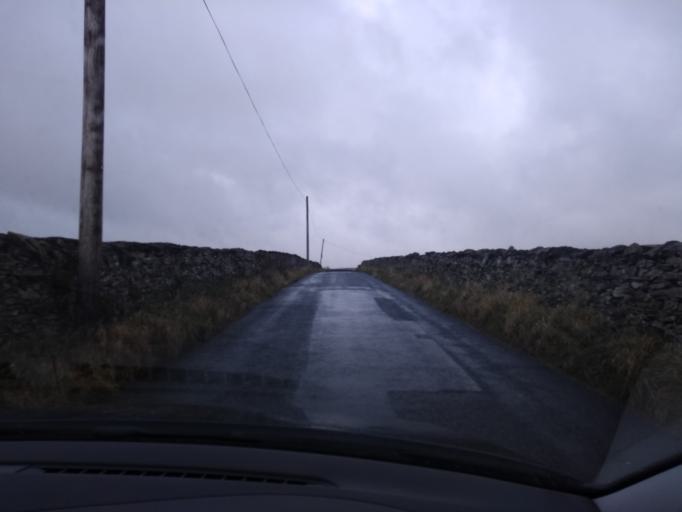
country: GB
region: England
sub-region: North Yorkshire
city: Settle
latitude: 54.1119
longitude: -2.2564
